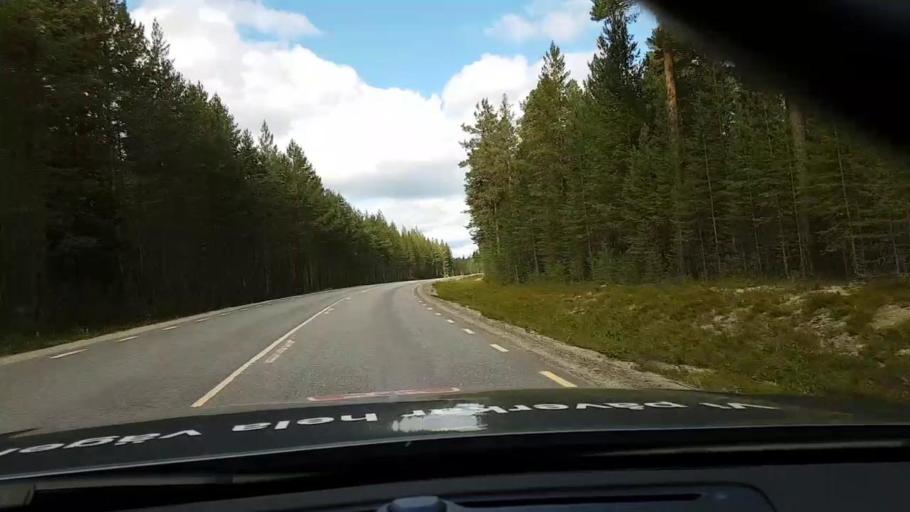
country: SE
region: Vaesternorrland
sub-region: OErnskoeldsviks Kommun
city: Bredbyn
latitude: 63.5325
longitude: 17.9677
